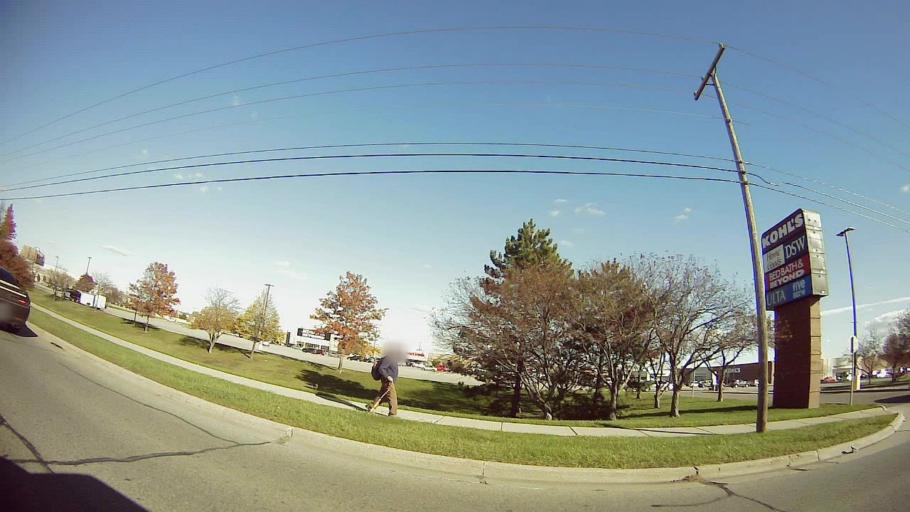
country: US
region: Michigan
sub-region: Oakland County
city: Clawson
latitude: 42.5396
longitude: -83.1071
